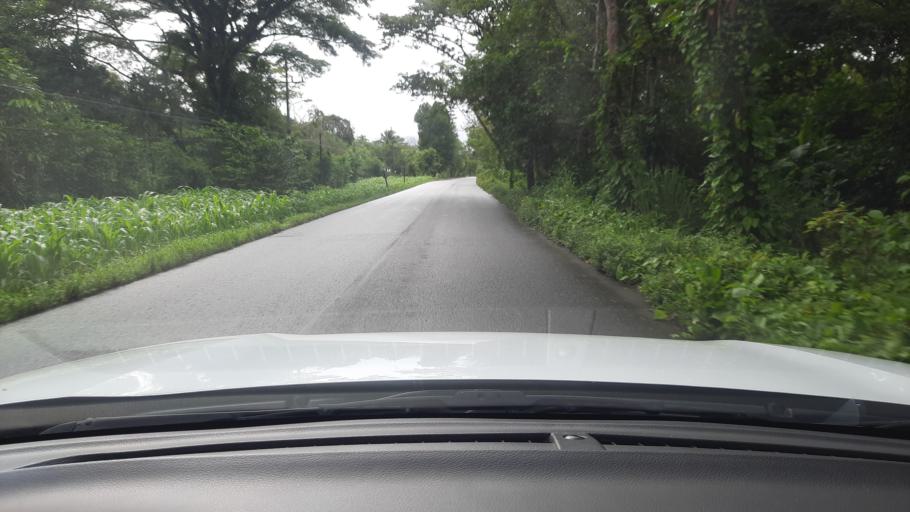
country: CR
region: Alajuela
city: San Jose
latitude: 10.9293
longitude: -85.0850
